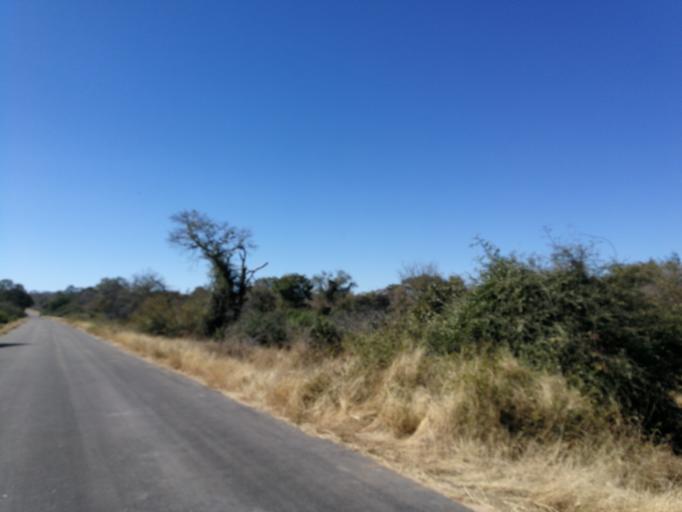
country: ZA
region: Limpopo
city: Thulamahashi
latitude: -24.9433
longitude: 31.6749
